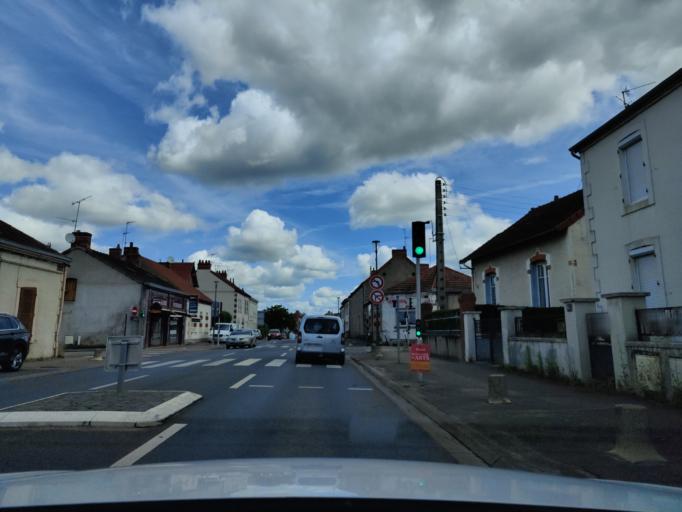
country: FR
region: Auvergne
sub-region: Departement de l'Allier
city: Desertines
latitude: 46.3518
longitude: 2.6128
